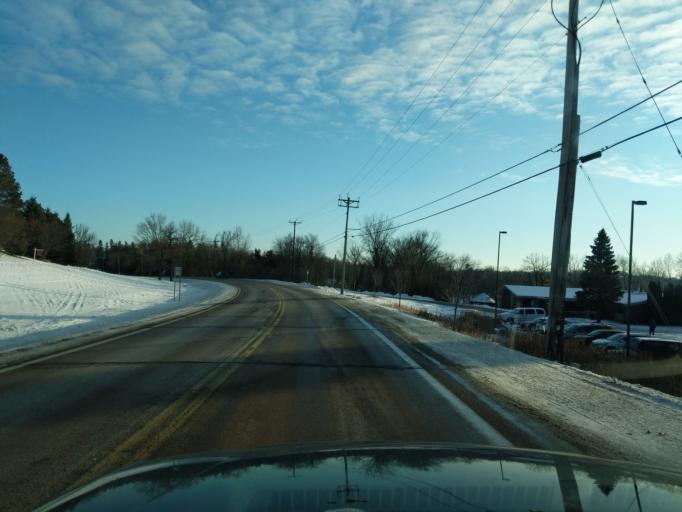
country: US
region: Minnesota
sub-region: Carver County
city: Victoria
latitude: 44.8752
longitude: -93.6413
